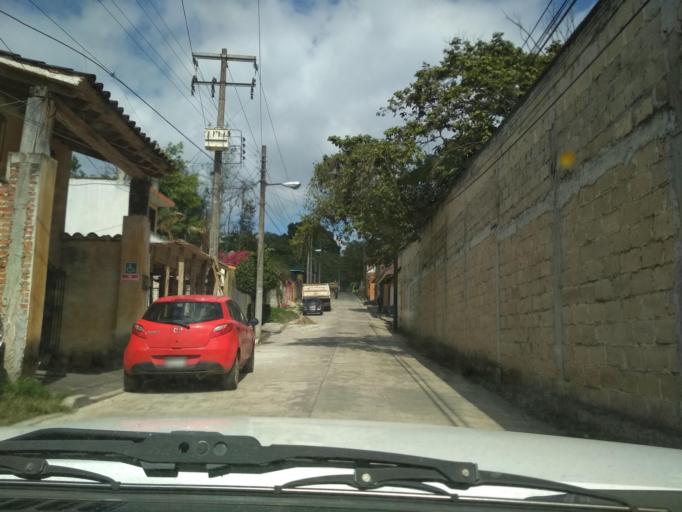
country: MX
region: Veracruz
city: Coatepec
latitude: 19.4515
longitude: -96.9448
